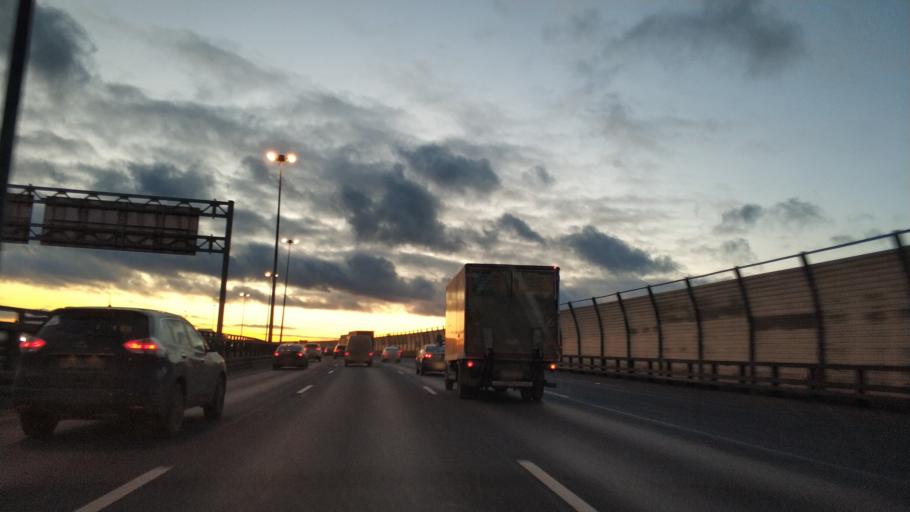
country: RU
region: St.-Petersburg
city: Obukhovo
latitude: 59.8491
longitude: 30.4631
